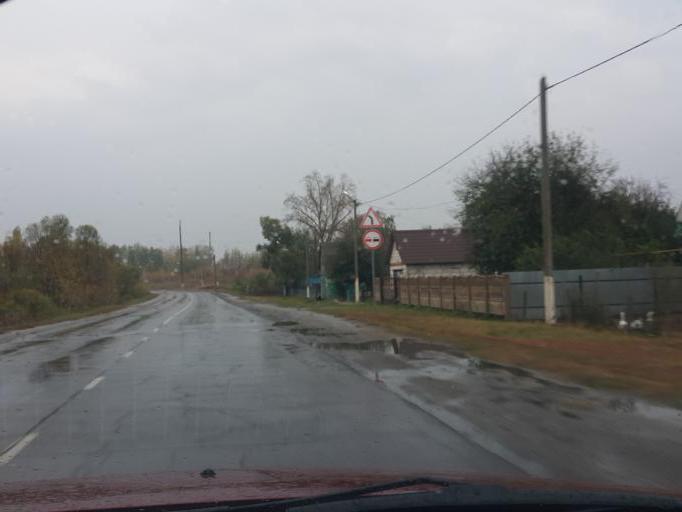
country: RU
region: Tambov
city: Znamenka
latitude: 52.4071
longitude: 41.4584
